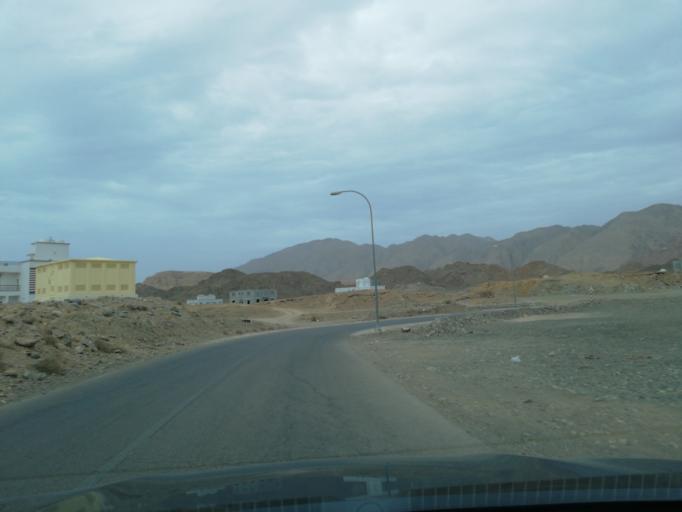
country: OM
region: Muhafazat Masqat
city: Bawshar
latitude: 23.4882
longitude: 58.3328
